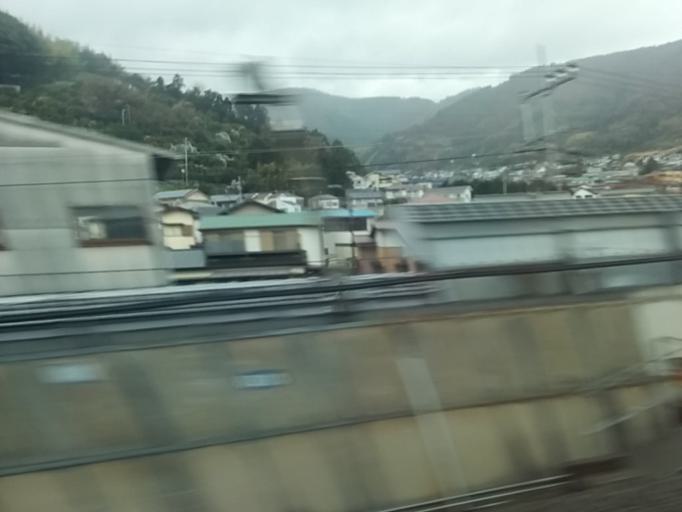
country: JP
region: Kanagawa
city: Yugawara
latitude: 35.1566
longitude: 139.1084
